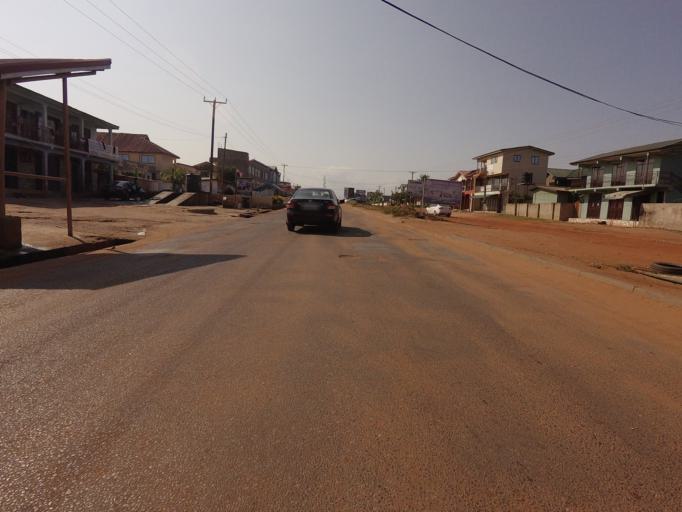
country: GH
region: Greater Accra
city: Teshi Old Town
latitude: 5.6063
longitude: -0.1059
